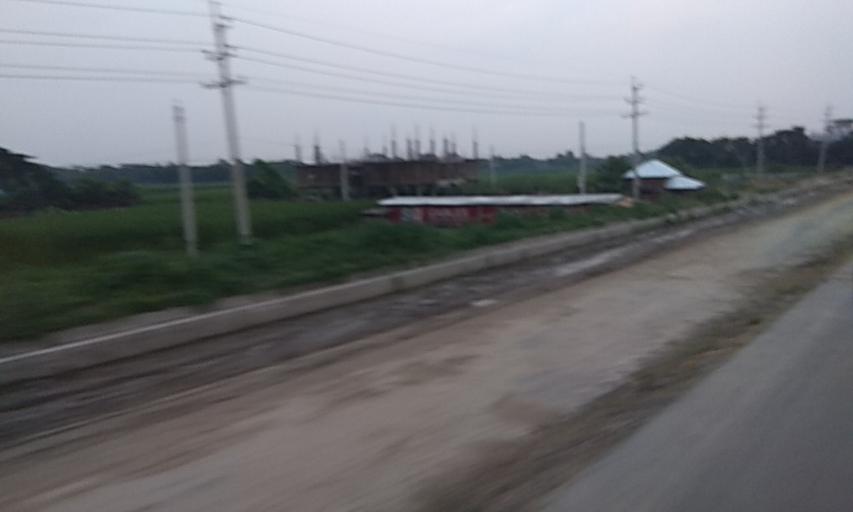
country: BD
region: Dhaka
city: Char Bhadrasan
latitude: 23.3742
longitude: 90.0264
